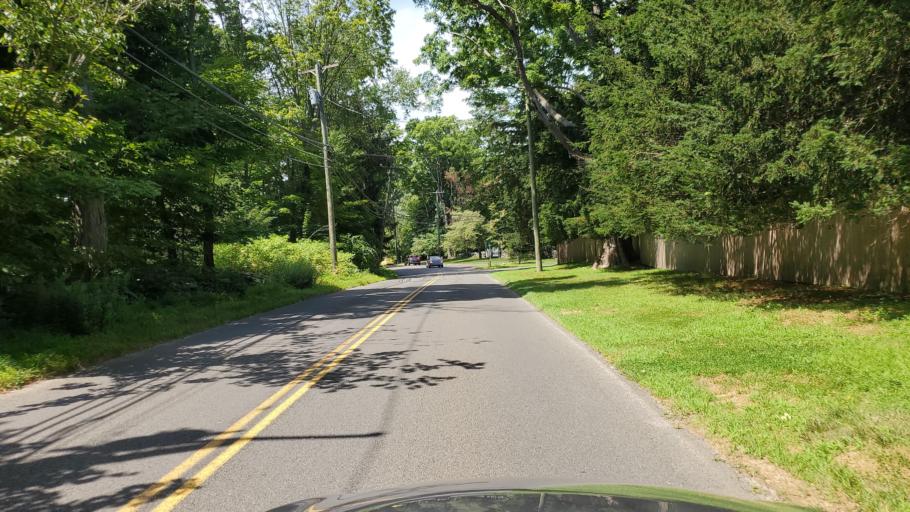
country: US
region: Connecticut
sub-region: Fairfield County
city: Southport
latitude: 41.1949
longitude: -73.3098
